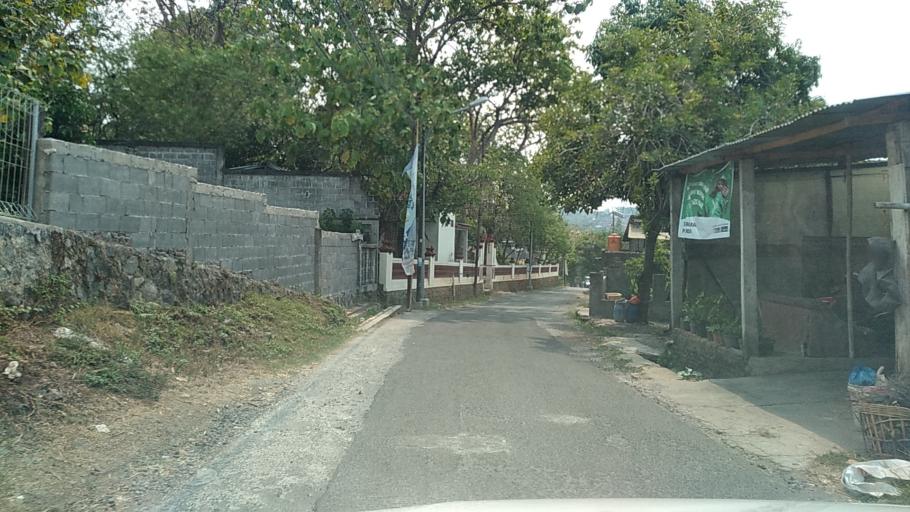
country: ID
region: Central Java
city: Semarang
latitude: -6.9969
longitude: 110.3339
